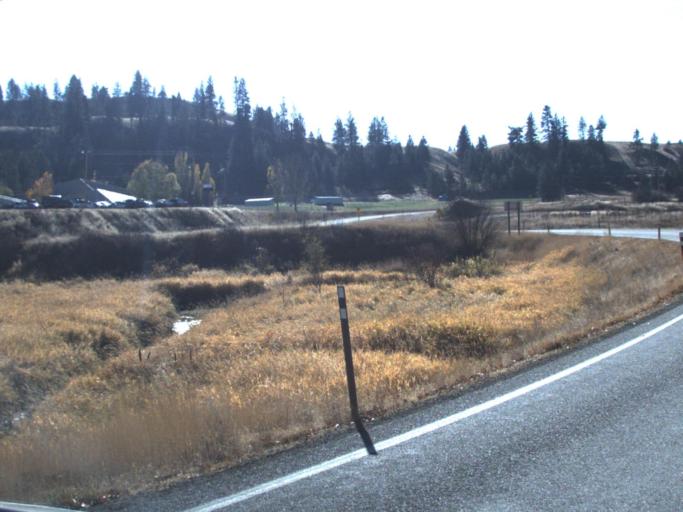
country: CA
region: British Columbia
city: Grand Forks
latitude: 48.8765
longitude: -118.6067
